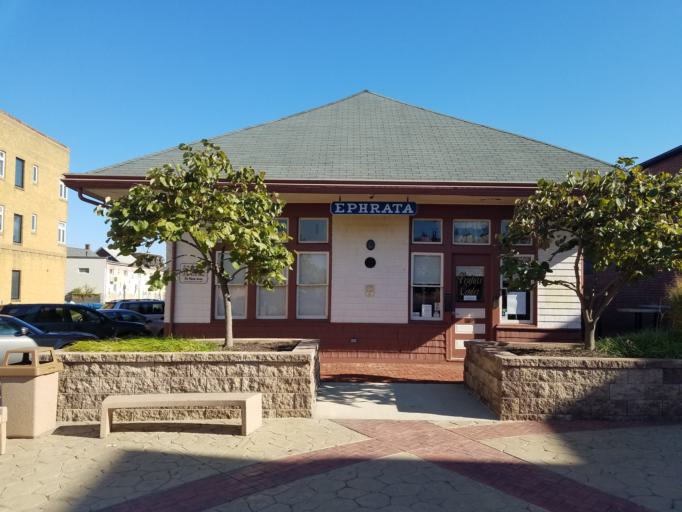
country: US
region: Pennsylvania
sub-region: Lancaster County
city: Ephrata
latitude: 40.1870
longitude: -76.1767
